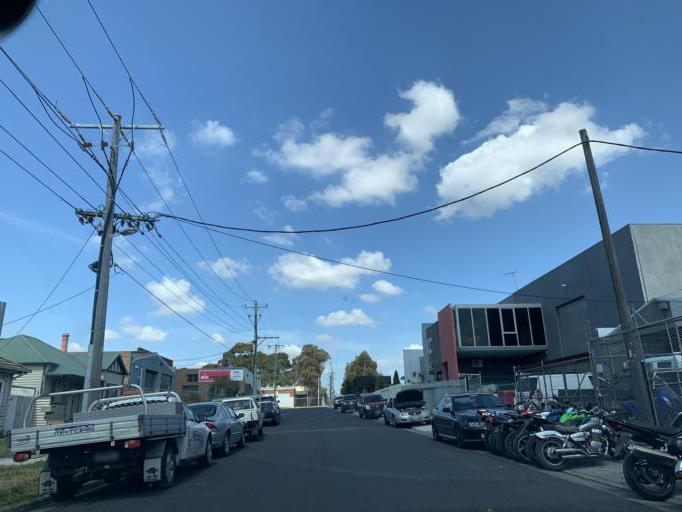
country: AU
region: Victoria
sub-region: Moreland
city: Coburg North
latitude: -37.7283
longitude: 144.9589
